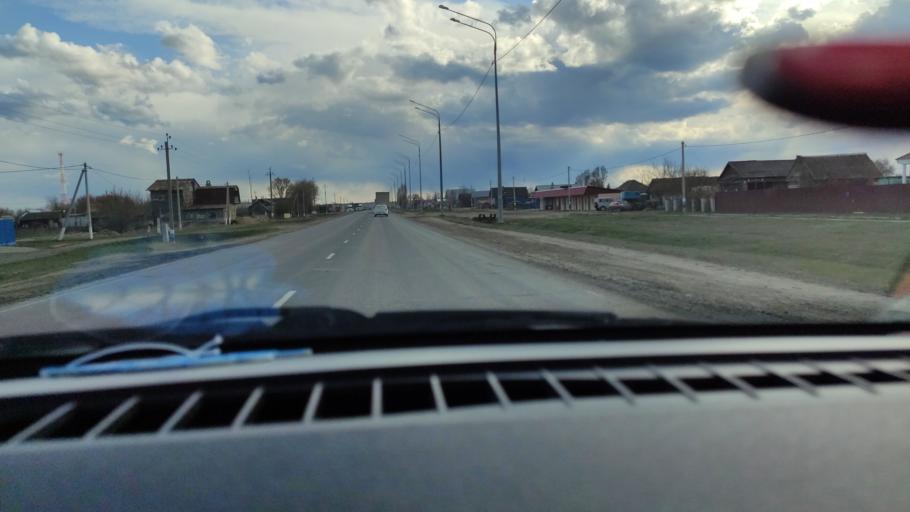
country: RU
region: Saratov
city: Sinodskoye
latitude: 51.9857
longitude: 46.6633
